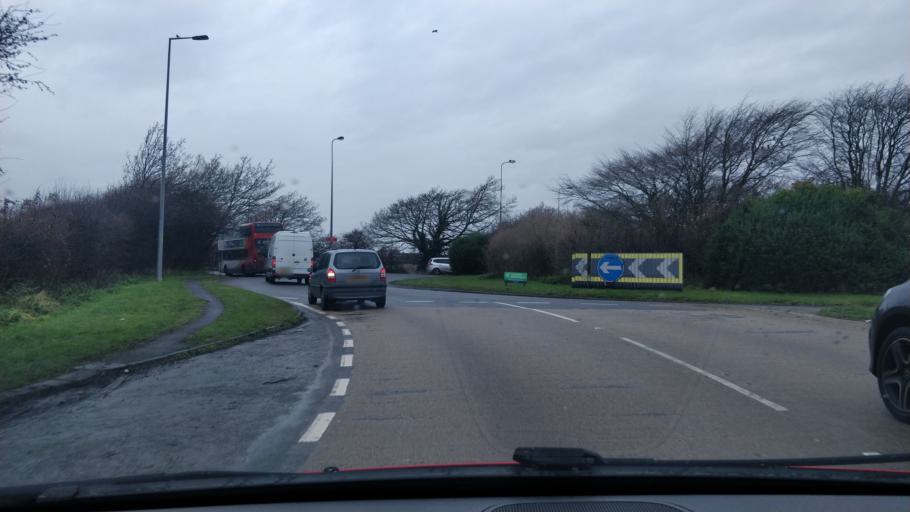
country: GB
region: England
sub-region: Sefton
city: Hightown
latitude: 53.5439
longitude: -3.0484
